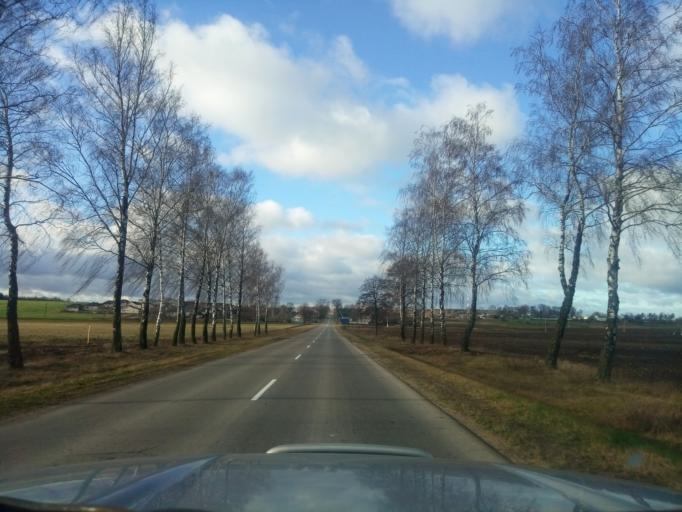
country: BY
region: Minsk
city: Tsimkavichy
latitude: 53.1750
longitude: 26.9724
